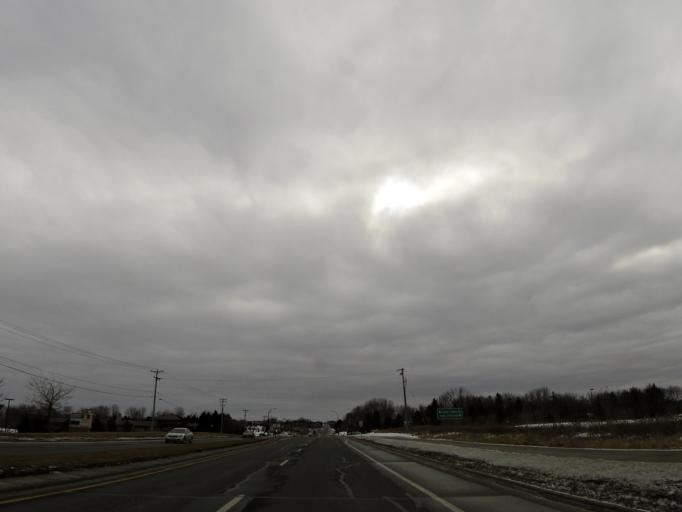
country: US
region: Minnesota
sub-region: Washington County
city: Woodbury
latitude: 44.9179
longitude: -92.9035
